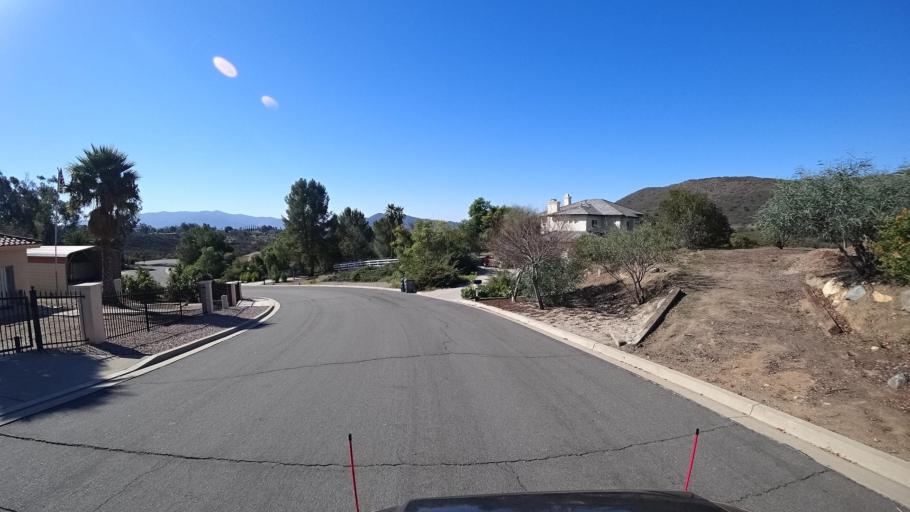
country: US
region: California
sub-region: San Diego County
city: Jamul
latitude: 32.7386
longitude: -116.8601
